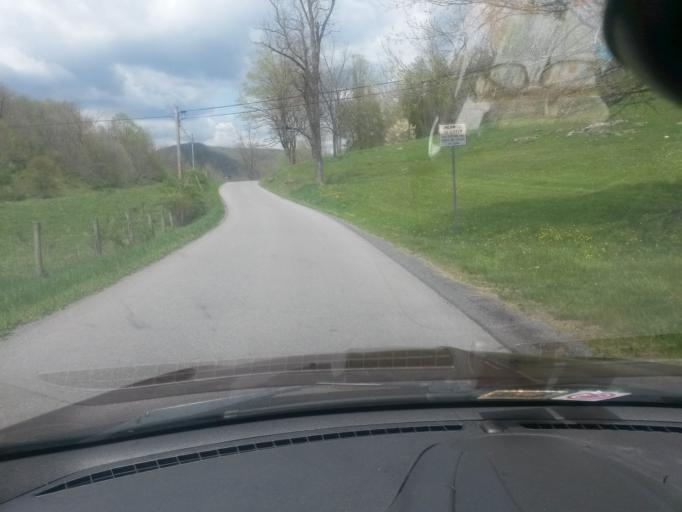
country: US
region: West Virginia
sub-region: Greenbrier County
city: White Sulphur Springs
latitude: 38.0346
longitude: -80.3324
